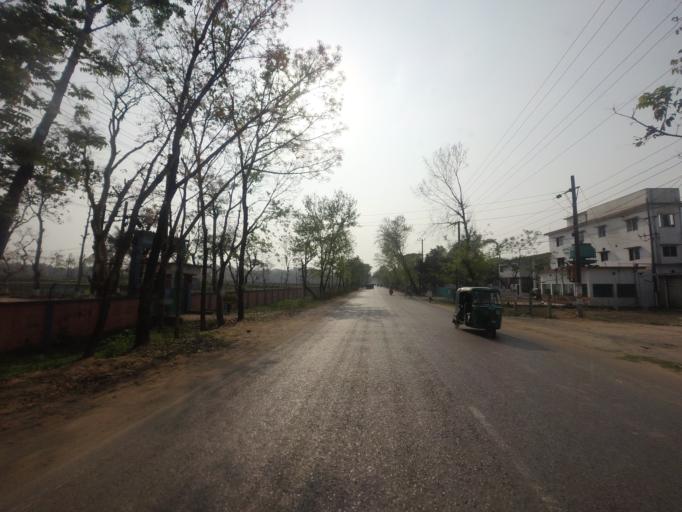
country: BD
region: Sylhet
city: Sylhet
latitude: 24.9149
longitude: 91.9442
